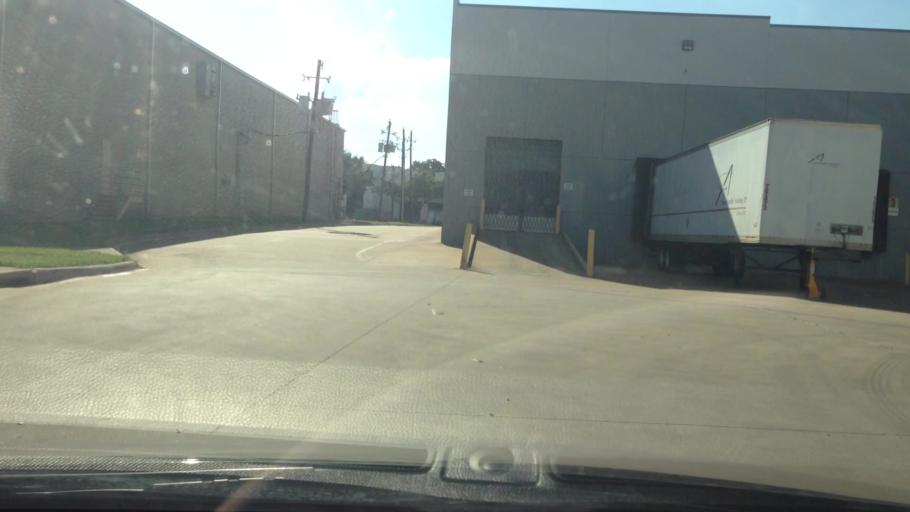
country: US
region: Texas
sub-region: Dallas County
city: Farmers Branch
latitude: 32.9182
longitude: -96.9040
